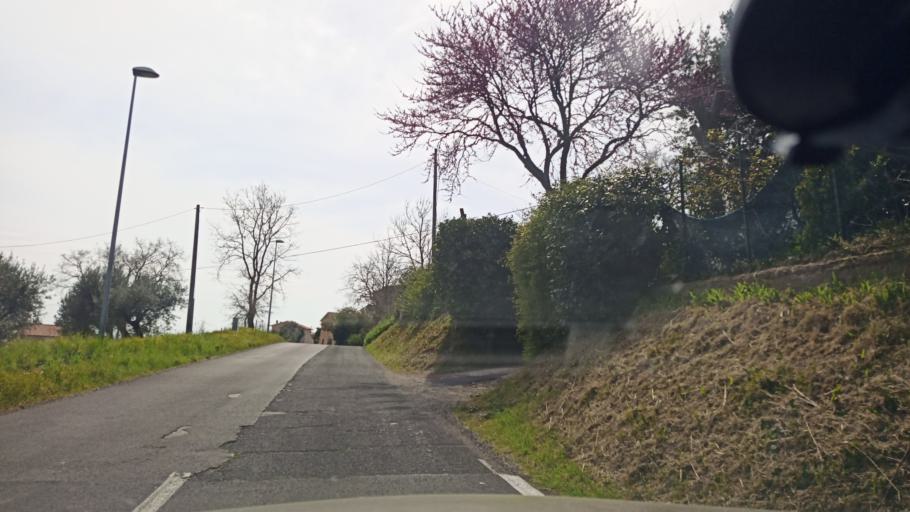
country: IT
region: Latium
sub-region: Provincia di Rieti
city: Torri in Sabina
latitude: 42.3398
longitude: 12.6505
